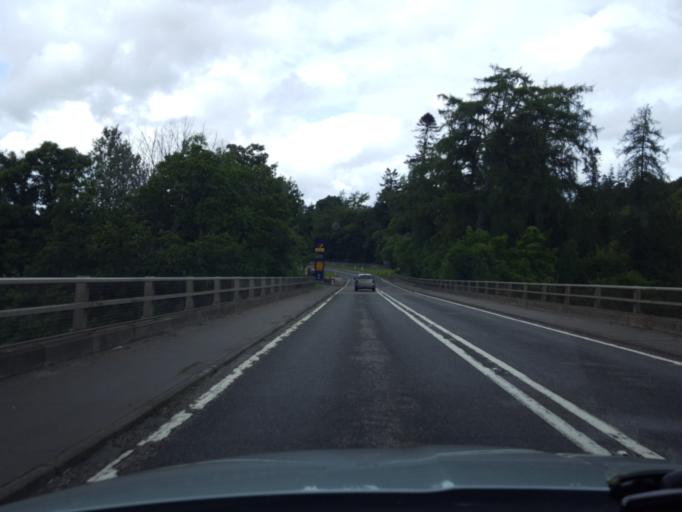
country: GB
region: Scotland
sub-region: Moray
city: Rothes
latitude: 57.4052
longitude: -3.3605
